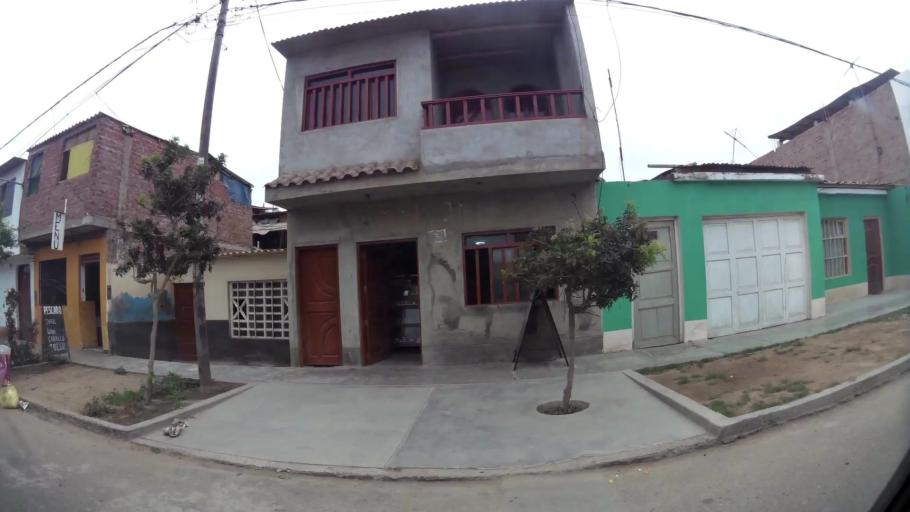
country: PE
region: La Libertad
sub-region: Provincia de Trujillo
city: Buenos Aires
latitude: -8.1458
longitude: -79.0493
